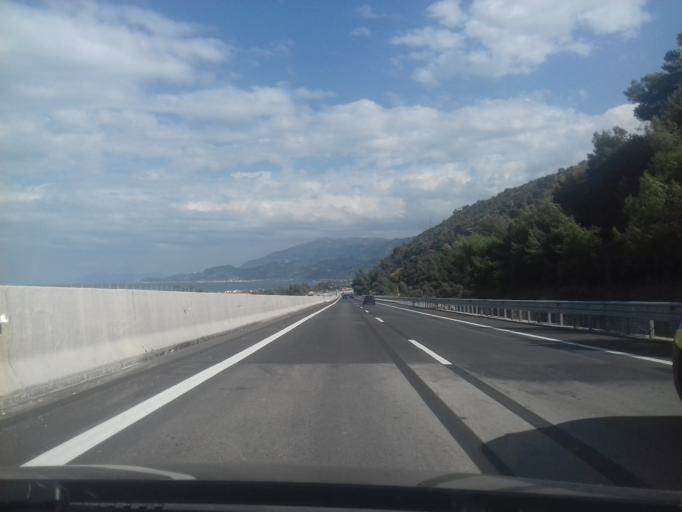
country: GR
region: West Greece
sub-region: Nomos Achaias
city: Siliveniotika
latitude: 38.1690
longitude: 22.3255
